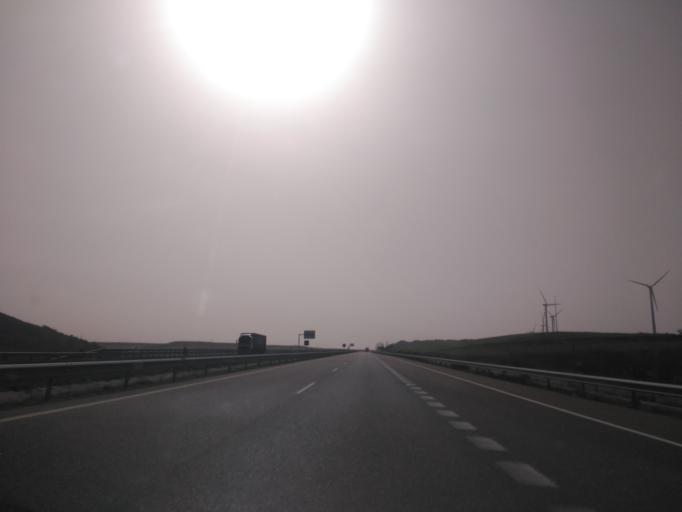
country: ES
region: Castille and Leon
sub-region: Provincia de Palencia
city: Monzon de Campos
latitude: 42.1112
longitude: -4.4810
